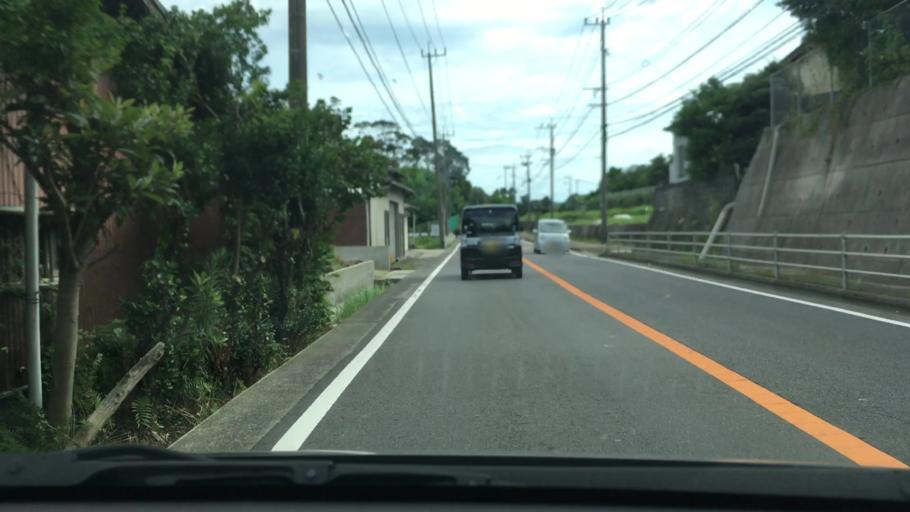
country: JP
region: Nagasaki
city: Togitsu
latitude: 32.8851
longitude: 129.7900
